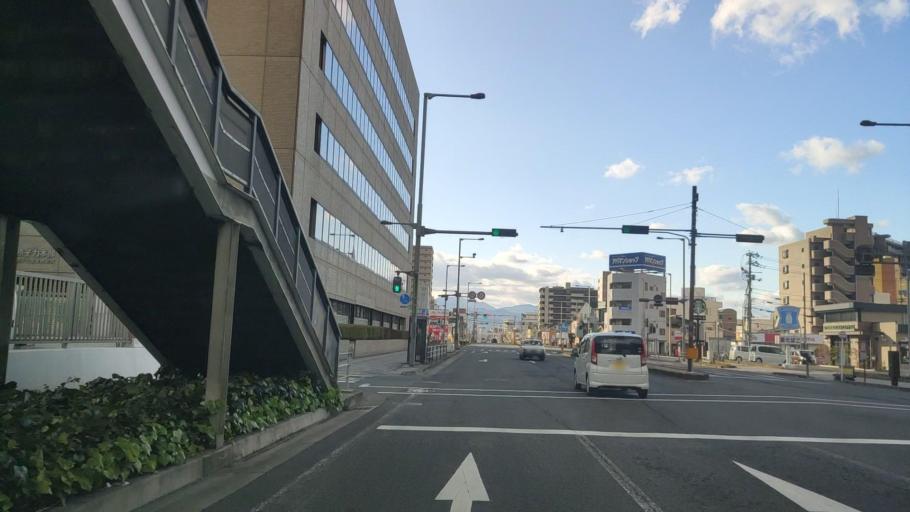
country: JP
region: Ehime
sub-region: Shikoku-chuo Shi
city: Matsuyama
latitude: 33.8360
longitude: 132.7588
